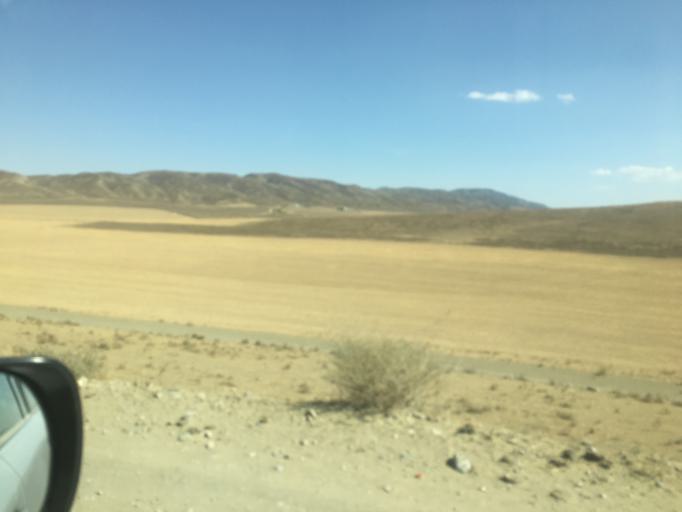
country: TM
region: Ahal
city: Baharly
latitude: 38.4290
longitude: 57.0321
